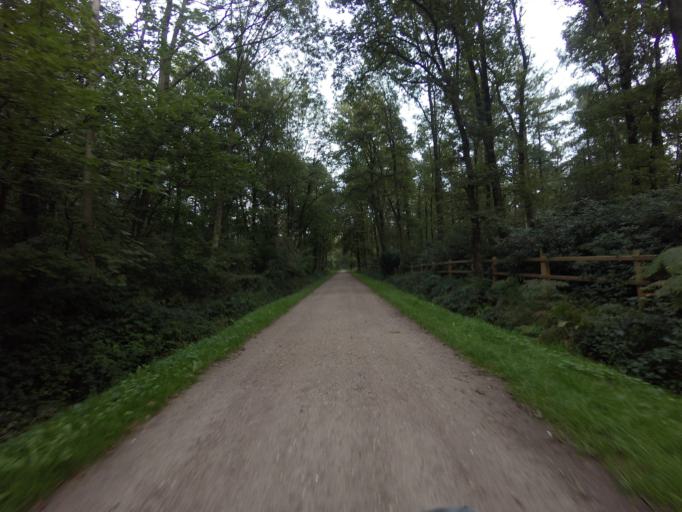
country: NL
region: Overijssel
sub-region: Gemeente Enschede
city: Enschede
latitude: 52.1943
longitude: 6.9106
